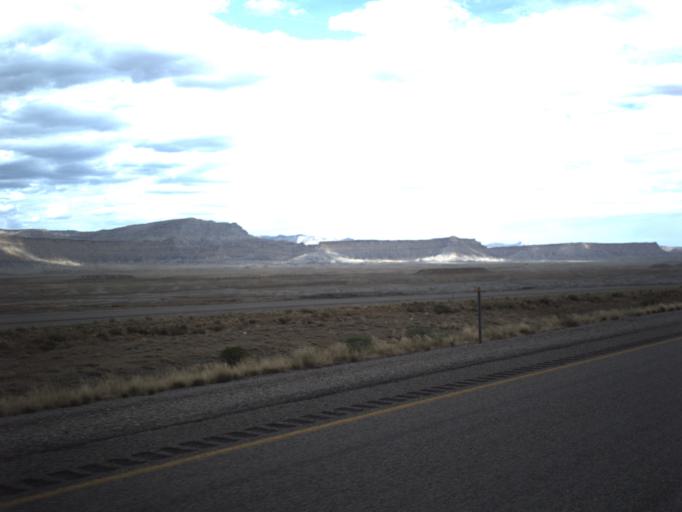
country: US
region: Utah
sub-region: Carbon County
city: East Carbon City
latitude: 38.9681
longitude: -110.0888
